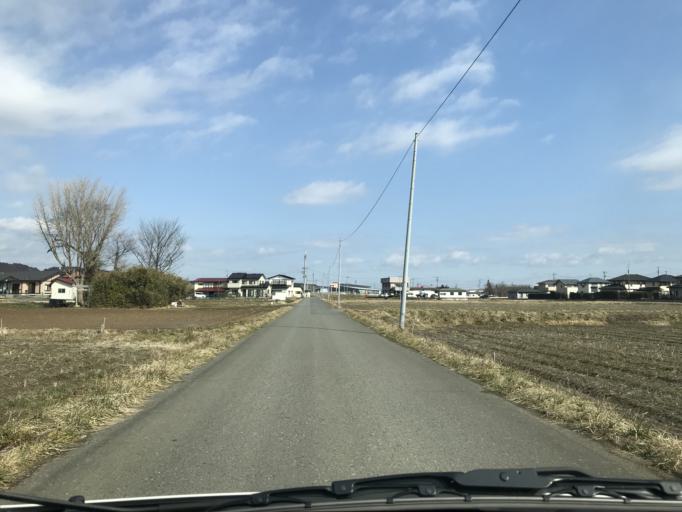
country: JP
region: Iwate
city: Mizusawa
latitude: 39.0410
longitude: 141.1284
